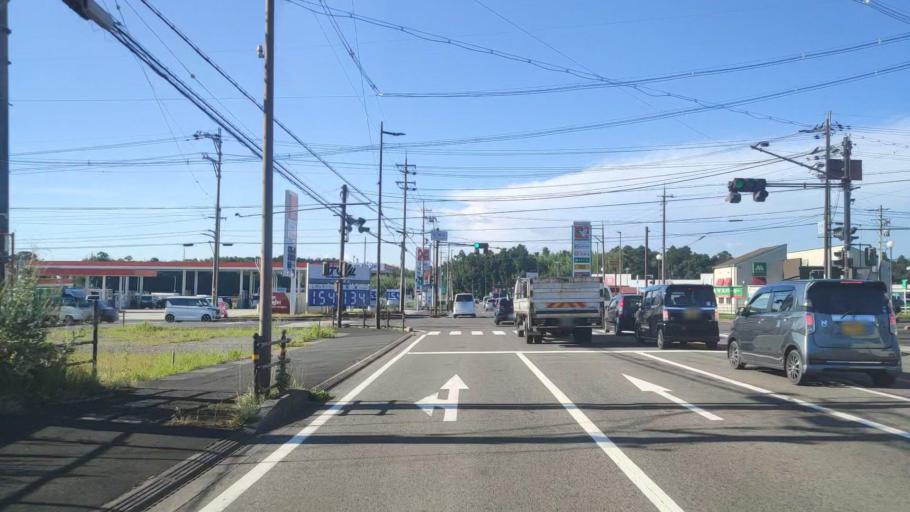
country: JP
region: Shiga Prefecture
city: Hino
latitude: 35.0201
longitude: 136.2388
